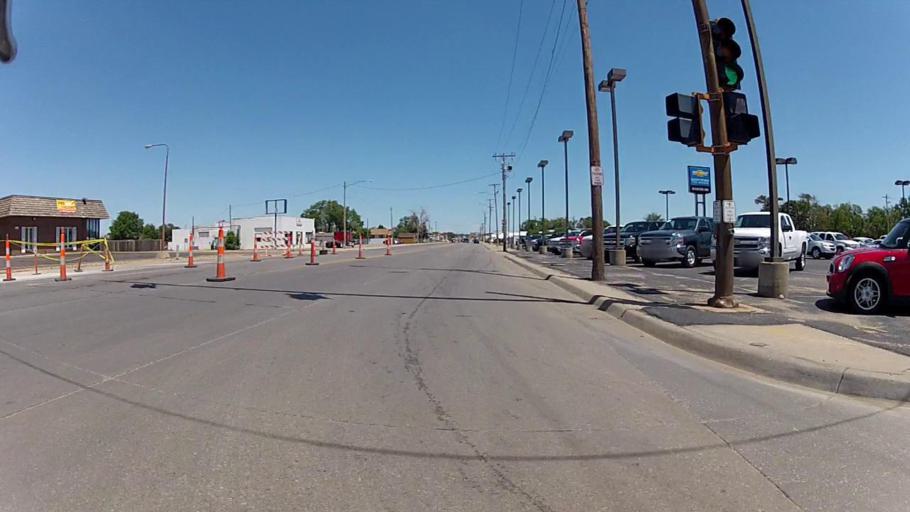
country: US
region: Kansas
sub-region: Ford County
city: Dodge City
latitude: 37.7364
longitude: -100.0194
